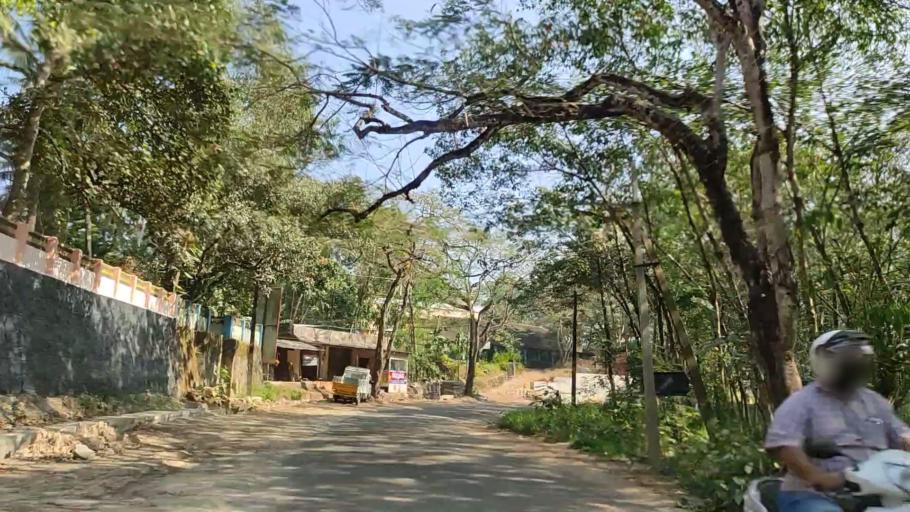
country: IN
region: Kerala
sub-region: Kollam
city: Punalur
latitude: 8.9055
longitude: 76.8745
